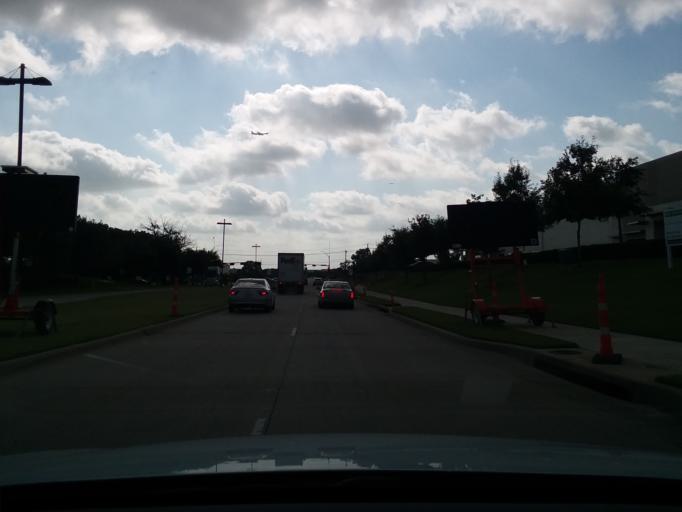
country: US
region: Texas
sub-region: Dallas County
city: Coppell
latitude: 32.9947
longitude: -97.0476
